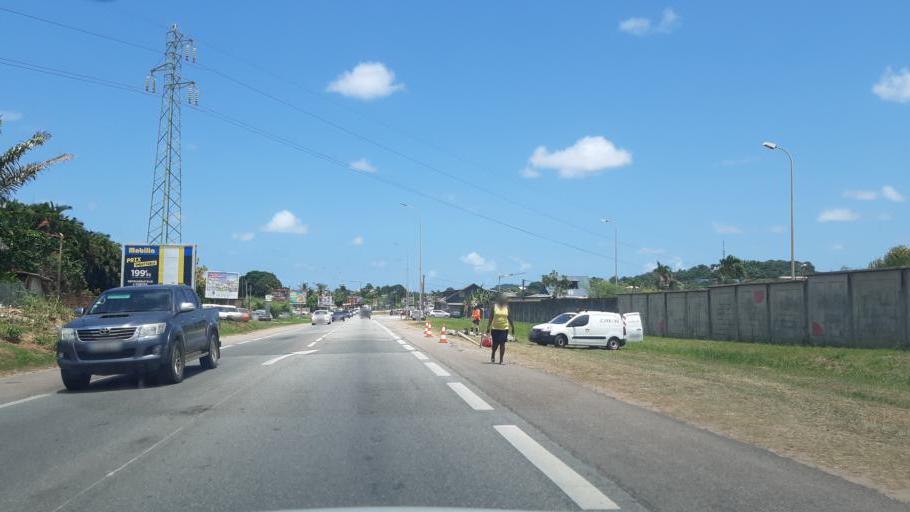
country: GF
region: Guyane
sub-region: Guyane
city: Cayenne
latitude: 4.9266
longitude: -52.3206
